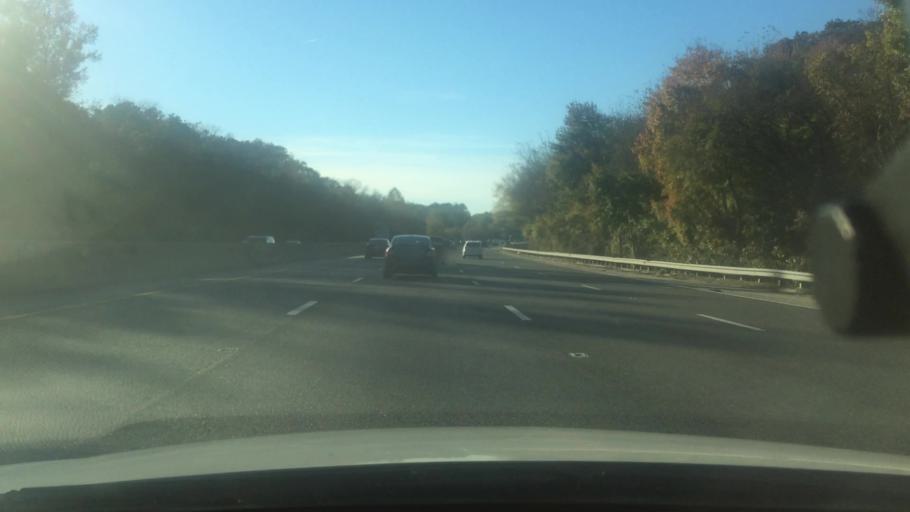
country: US
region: North Carolina
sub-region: Orange County
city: Chapel Hill
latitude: 35.9039
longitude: -78.9654
